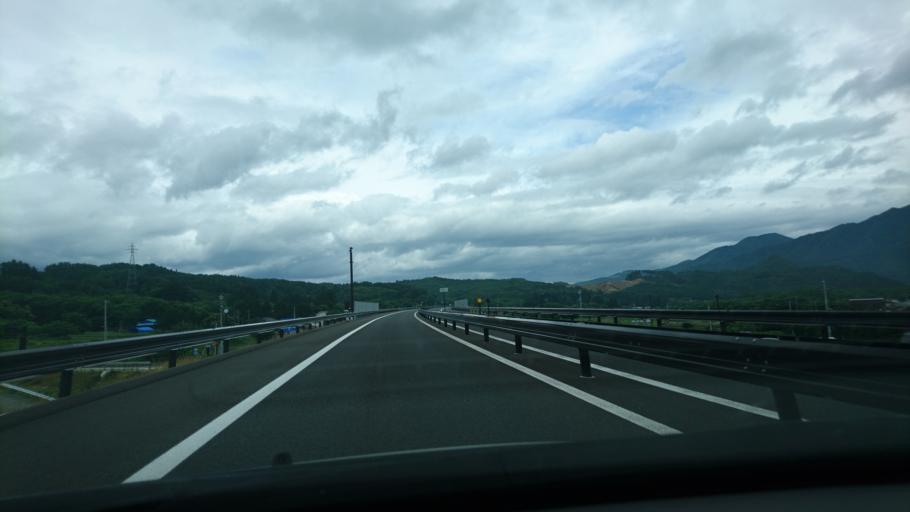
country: JP
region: Iwate
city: Yamada
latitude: 39.5396
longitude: 141.9200
